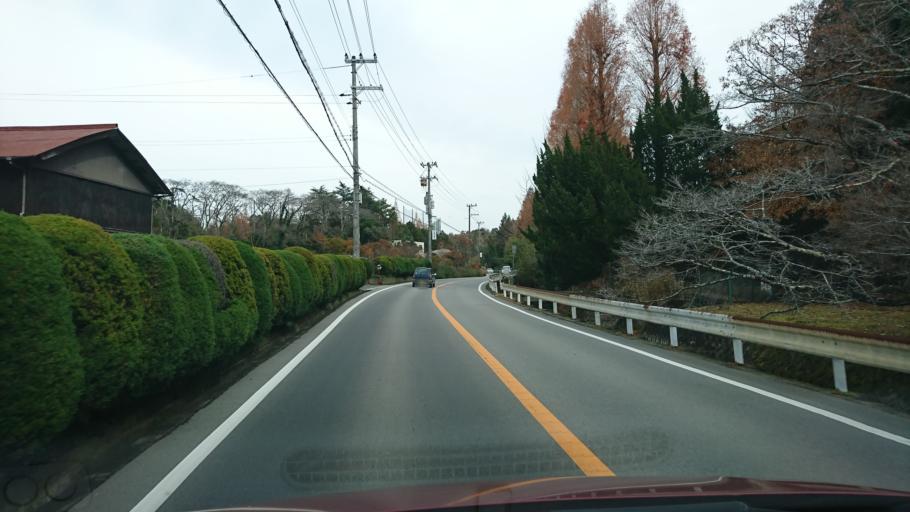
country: JP
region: Osaka
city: Ikeda
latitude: 34.8811
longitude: 135.4244
